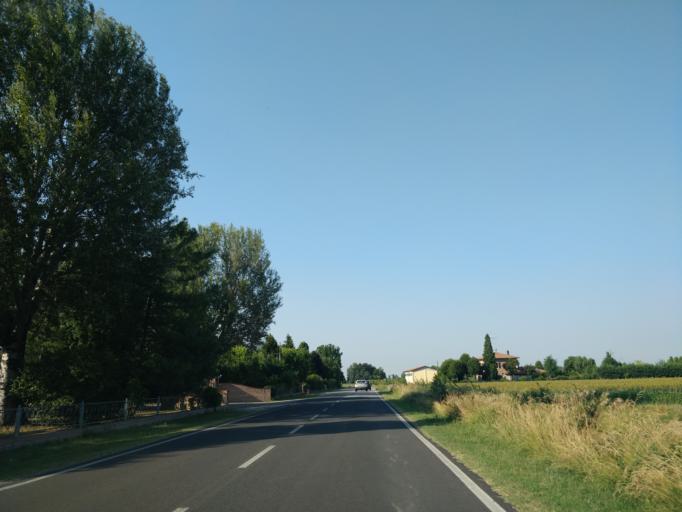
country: IT
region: Emilia-Romagna
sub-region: Provincia di Bologna
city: Argelato
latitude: 44.6308
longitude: 11.3423
